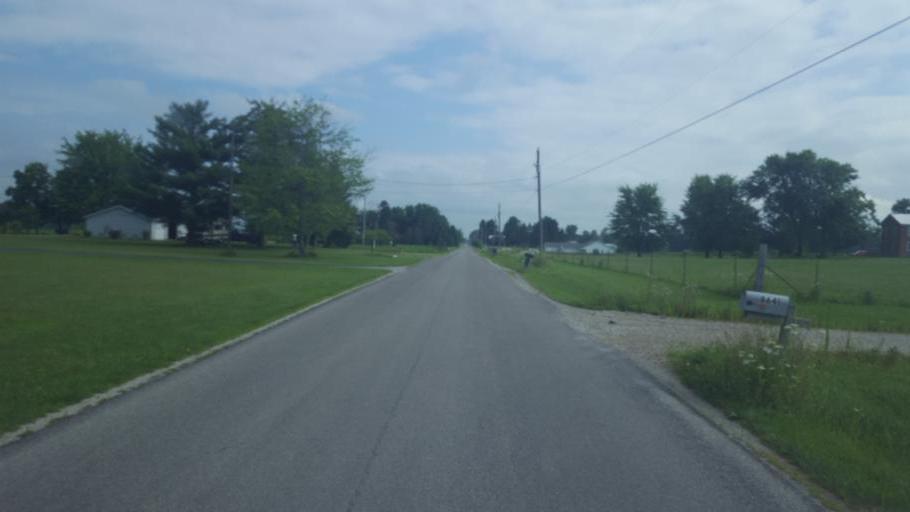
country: US
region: Ohio
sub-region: Crawford County
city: Galion
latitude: 40.6700
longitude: -82.7843
